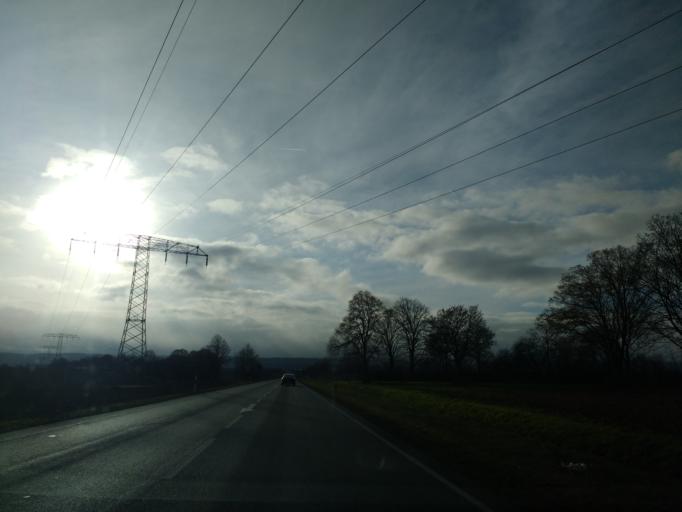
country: DE
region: Saxony-Anhalt
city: Quedlinburg
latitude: 51.7726
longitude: 11.1588
